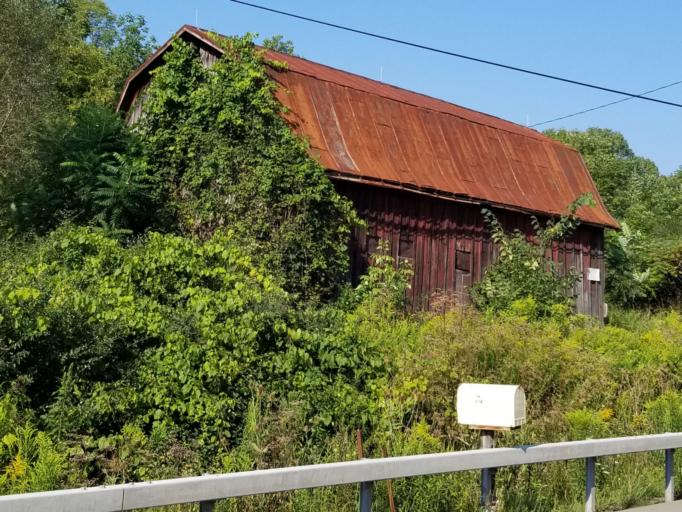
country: US
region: New York
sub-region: Allegany County
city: Belmont
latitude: 42.2959
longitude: -78.0764
